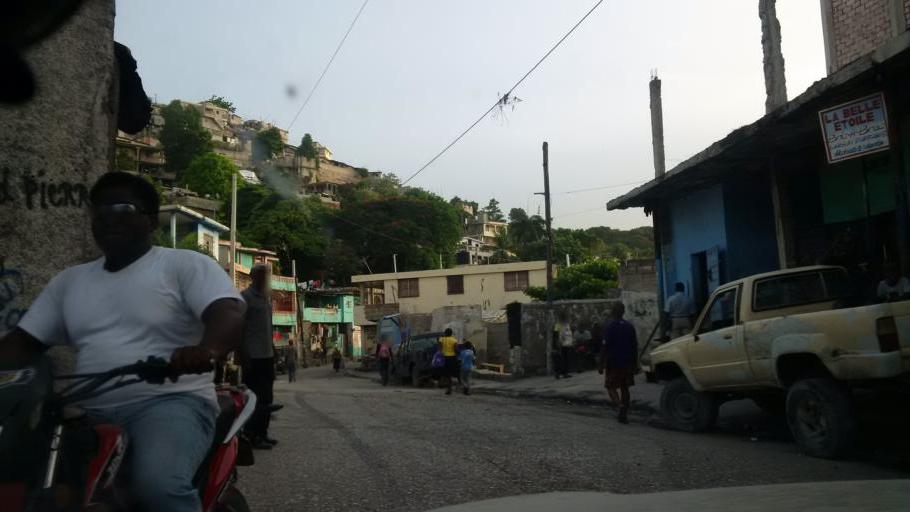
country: HT
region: Ouest
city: Port-au-Prince
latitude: 18.5283
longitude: -72.3496
